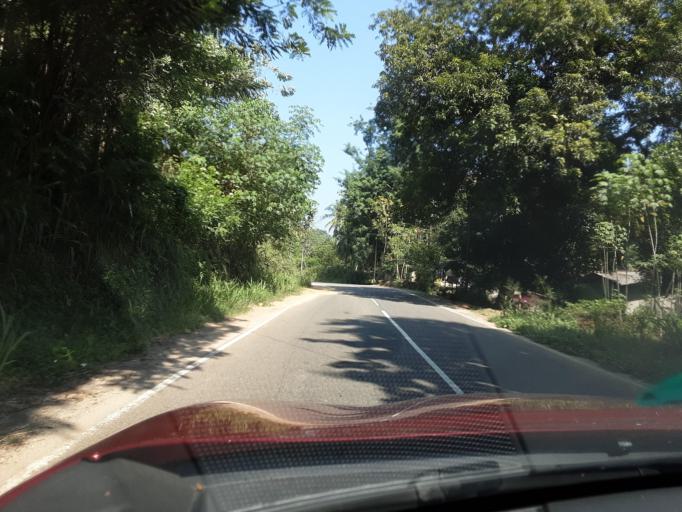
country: LK
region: Uva
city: Badulla
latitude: 7.1585
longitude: 81.0524
